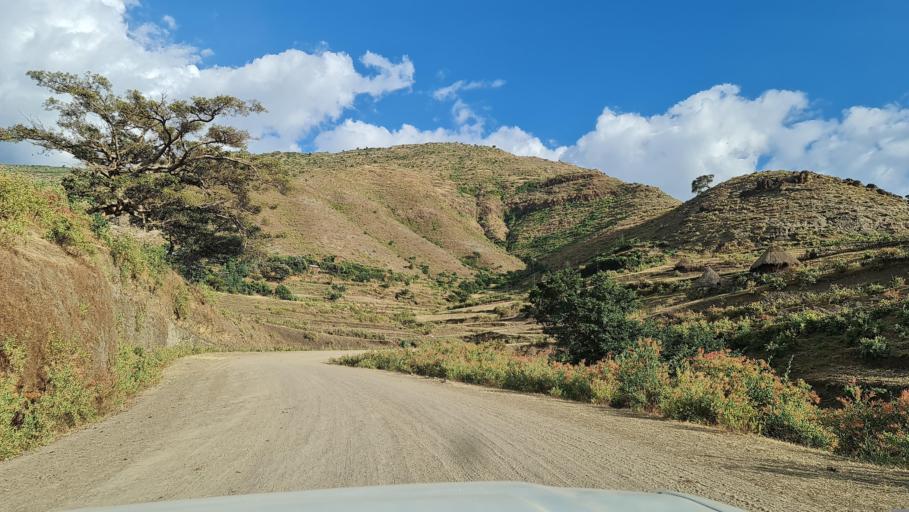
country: ET
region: Amhara
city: Debark'
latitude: 13.0576
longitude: 38.0182
